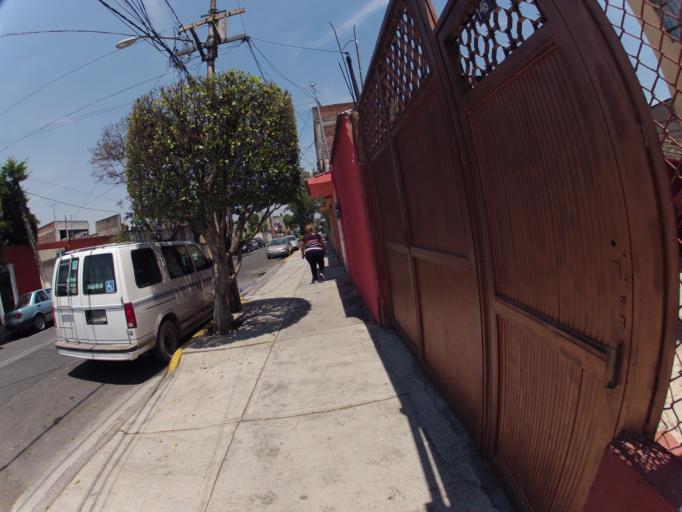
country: MX
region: Mexico City
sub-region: Iztacalco
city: Iztacalco
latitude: 19.4102
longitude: -99.0915
